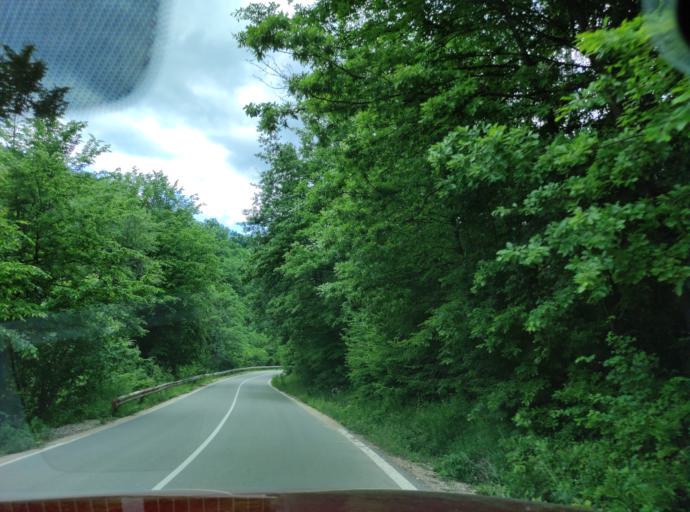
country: BG
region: Montana
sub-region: Obshtina Chiprovtsi
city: Chiprovtsi
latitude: 43.4638
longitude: 22.8844
